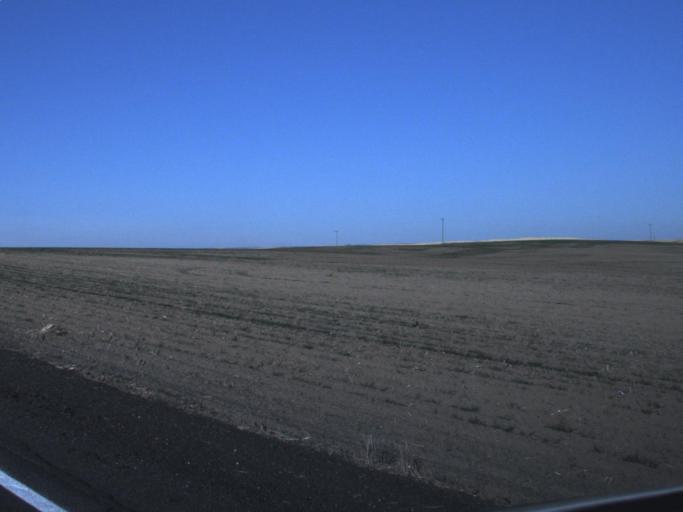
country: US
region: Washington
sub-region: Adams County
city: Ritzville
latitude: 47.0270
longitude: -118.3499
